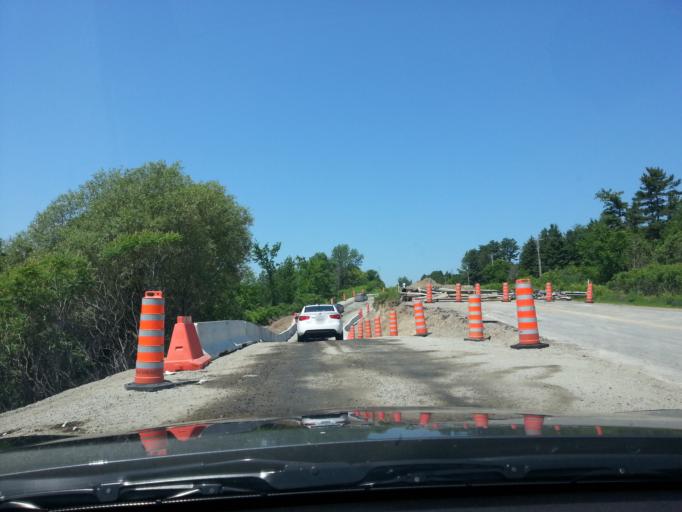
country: CA
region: Quebec
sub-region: Outaouais
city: Wakefield
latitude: 45.5444
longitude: -76.0544
